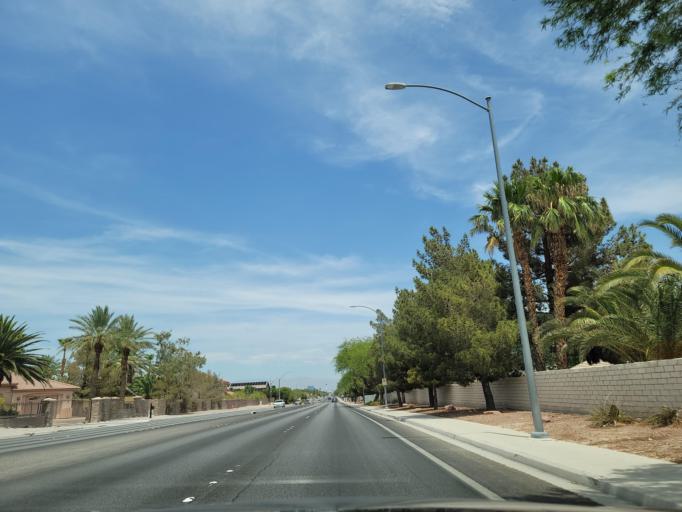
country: US
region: Nevada
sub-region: Clark County
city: Paradise
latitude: 36.0331
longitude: -115.1544
